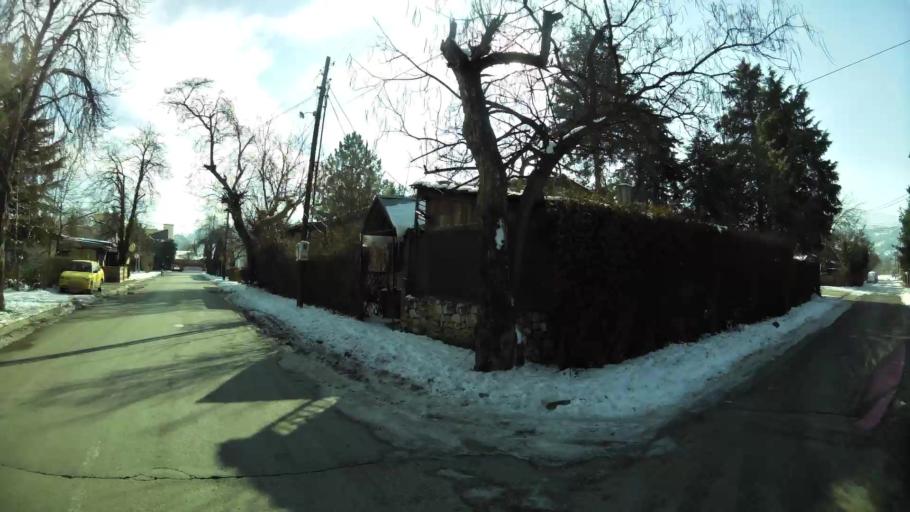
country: MK
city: Krushopek
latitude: 42.0020
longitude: 21.3731
